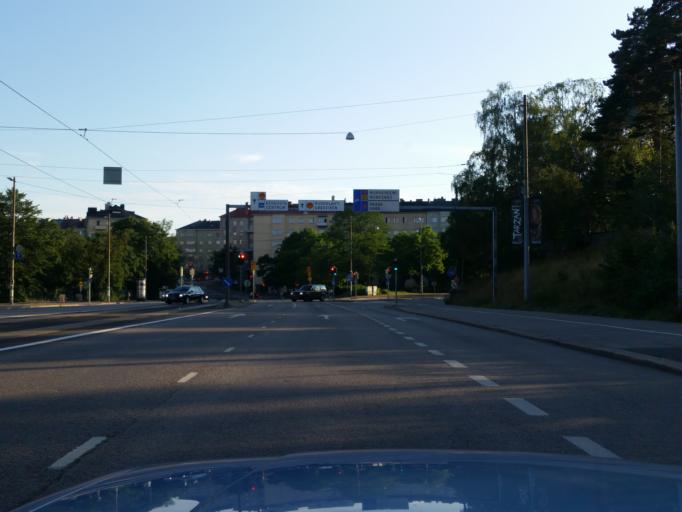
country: FI
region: Uusimaa
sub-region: Helsinki
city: Helsinki
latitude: 60.1904
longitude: 24.9217
